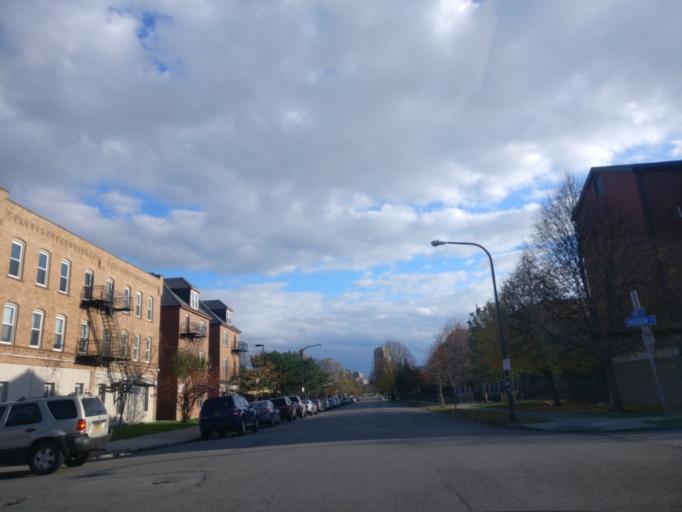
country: US
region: New York
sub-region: Erie County
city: Buffalo
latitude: 42.8955
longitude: -78.8901
